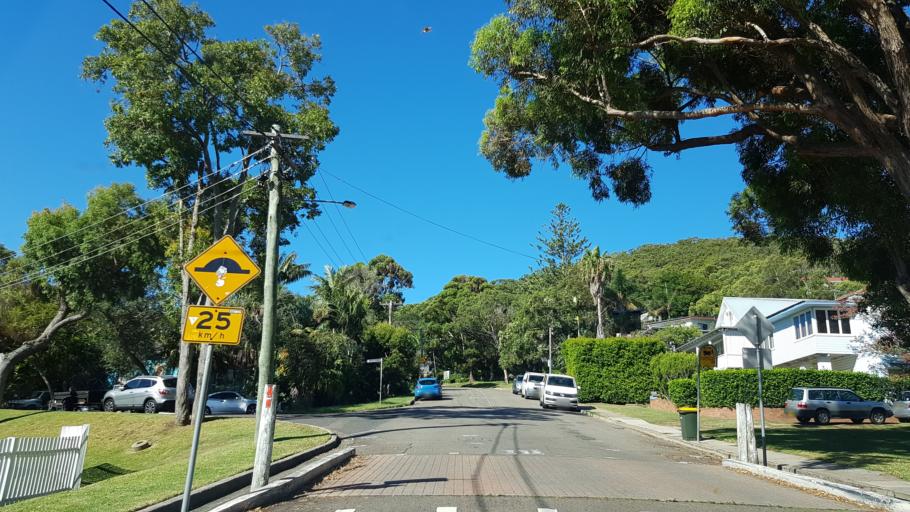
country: AU
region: New South Wales
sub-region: Pittwater
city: Bilgola Beach
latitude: -33.6230
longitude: 151.3369
